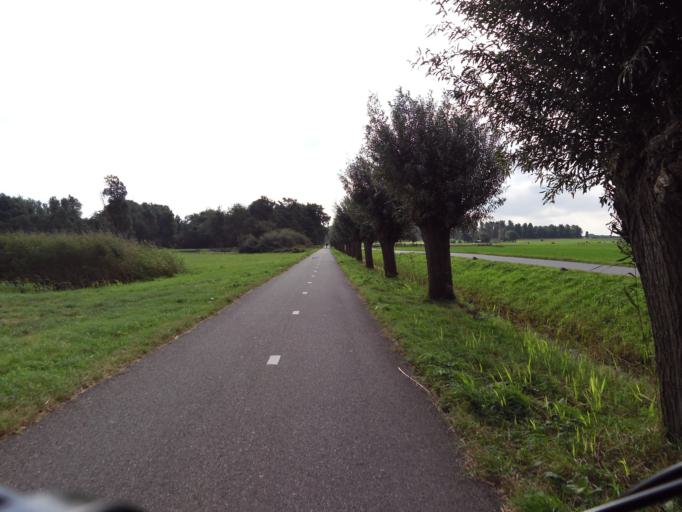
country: NL
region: South Holland
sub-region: Gemeente Zoetermeer
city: Zoetermeer
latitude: 52.0981
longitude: 4.5009
